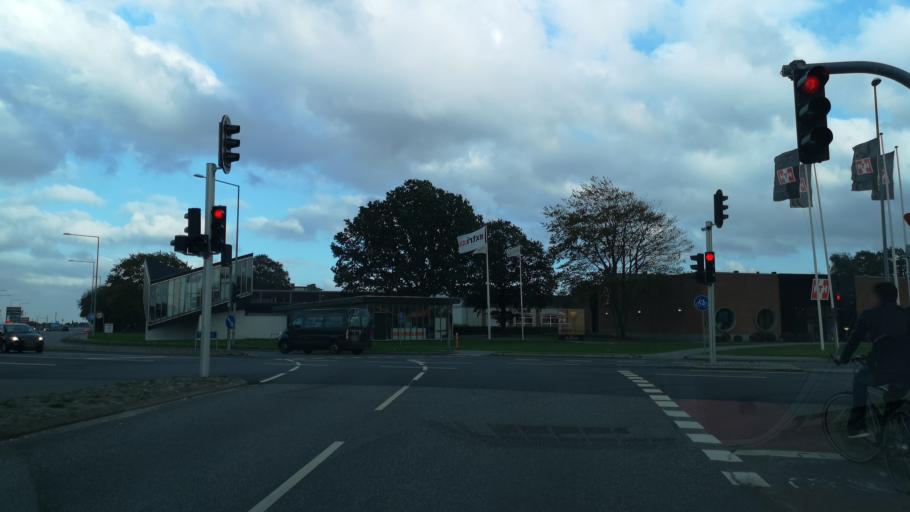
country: DK
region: Central Jutland
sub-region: Herning Kommune
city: Herning
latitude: 56.1347
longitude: 8.9931
